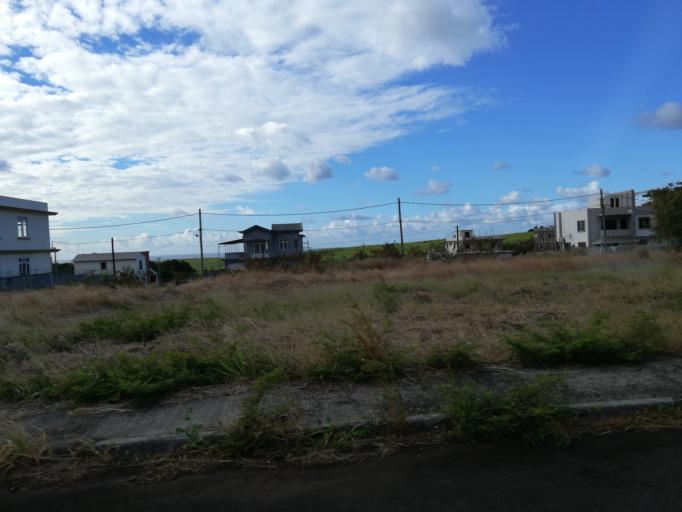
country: MU
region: Black River
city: Petite Riviere
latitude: -20.2006
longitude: 57.4630
